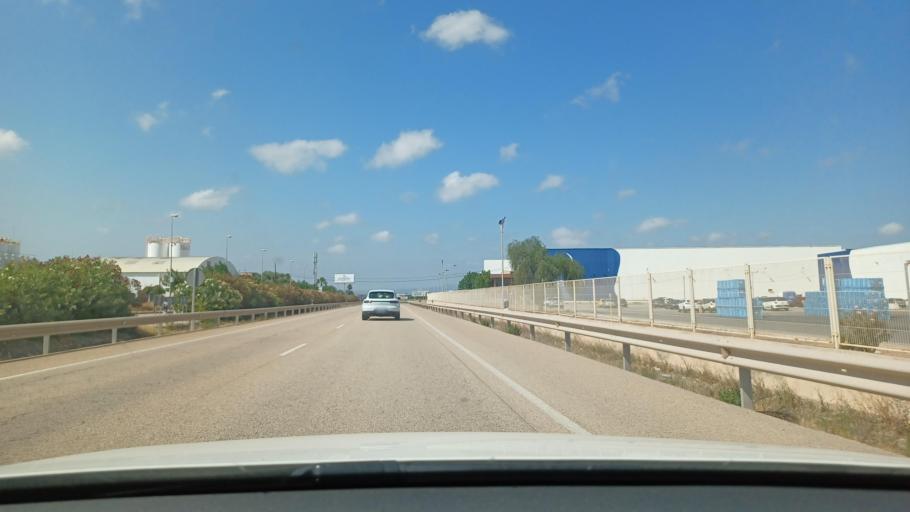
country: ES
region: Valencia
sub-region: Provincia de Castello
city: Moncofar
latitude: 39.8266
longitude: -0.1652
